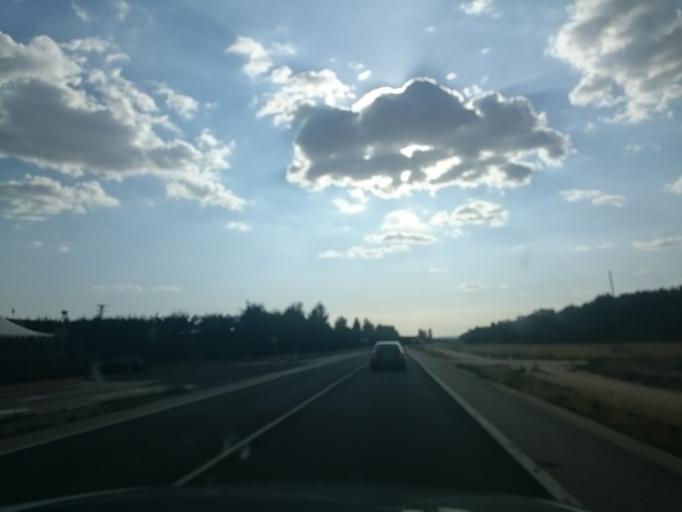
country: ES
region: Castille and Leon
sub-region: Provincia de Burgos
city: Los Tomillares
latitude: 42.3334
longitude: -3.5650
